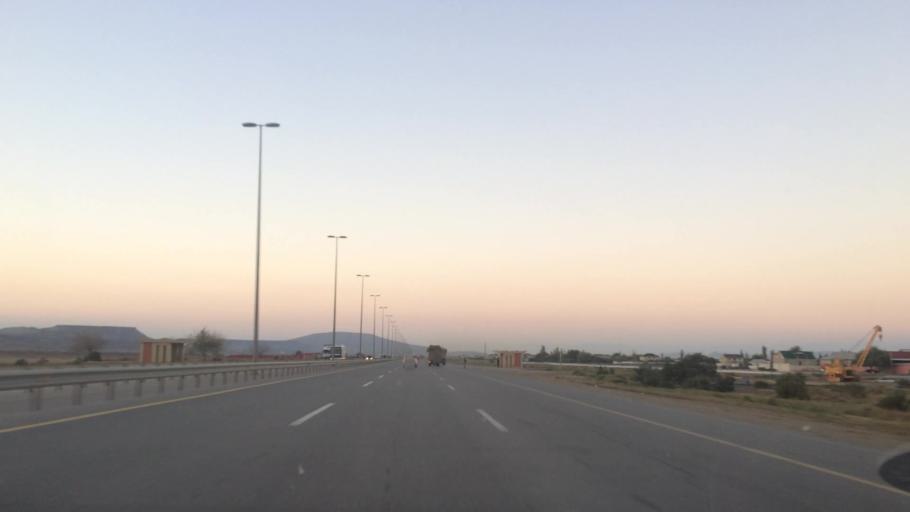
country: AZ
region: Baki
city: Qobustan
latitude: 40.0156
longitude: 49.4262
